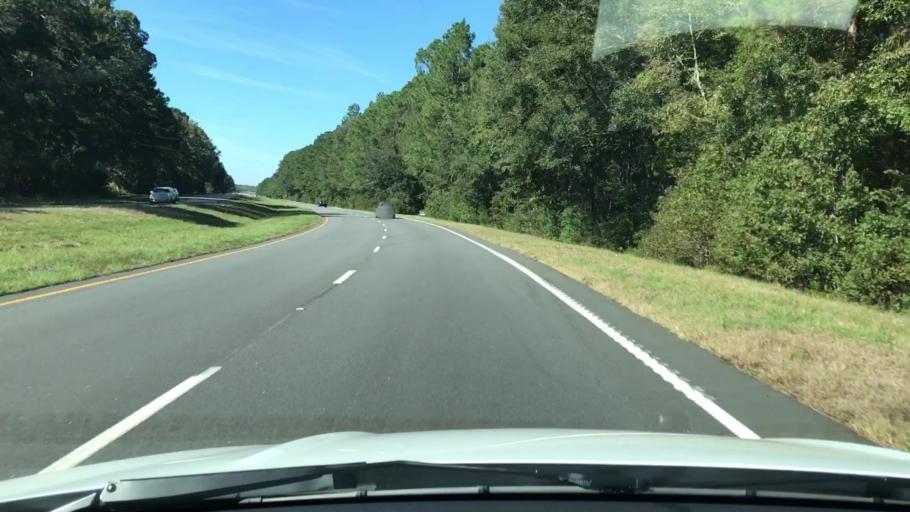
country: US
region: South Carolina
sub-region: Beaufort County
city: Laurel Bay
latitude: 32.5863
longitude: -80.7438
